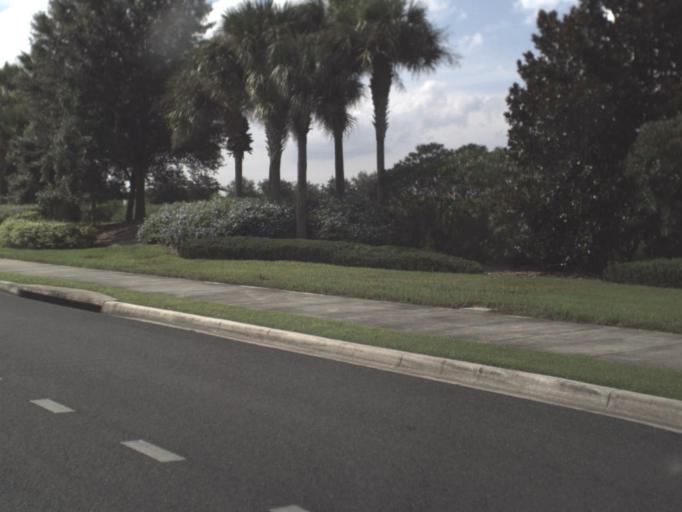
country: US
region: Florida
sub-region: Manatee County
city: Ellenton
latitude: 27.4862
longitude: -82.4557
